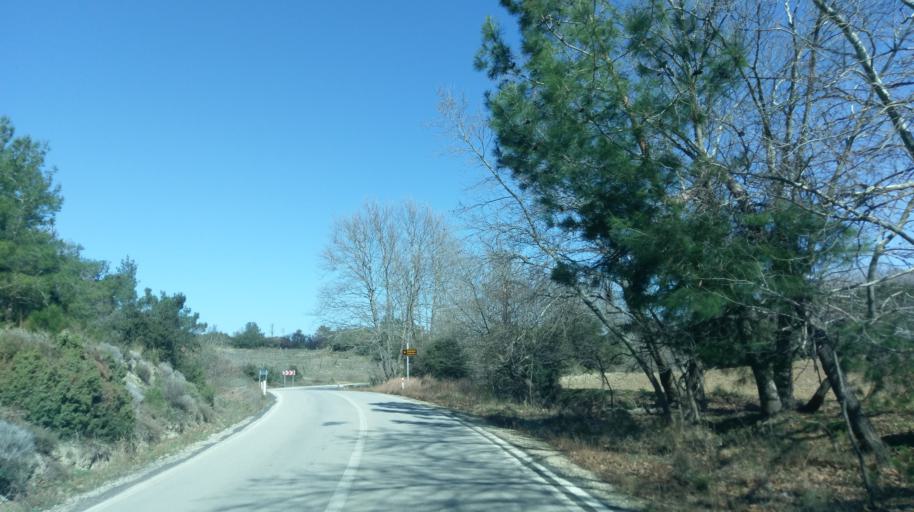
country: TR
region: Canakkale
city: Eceabat
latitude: 40.1209
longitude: 26.2568
